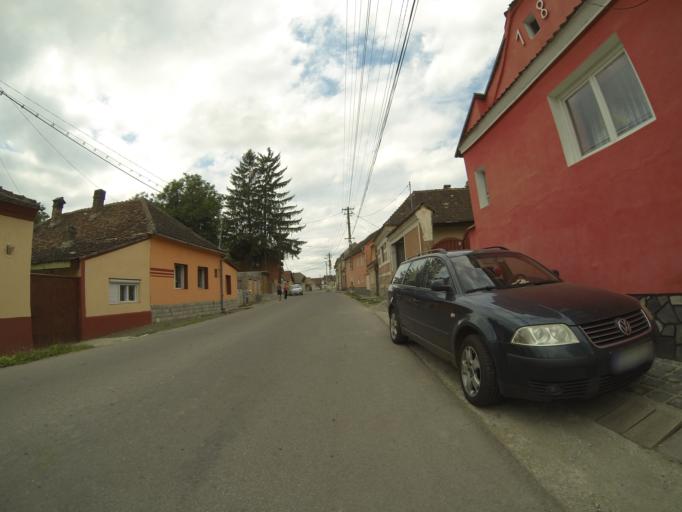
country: RO
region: Brasov
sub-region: Comuna Hoghiz
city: Hoghiz
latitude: 46.0239
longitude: 25.4149
